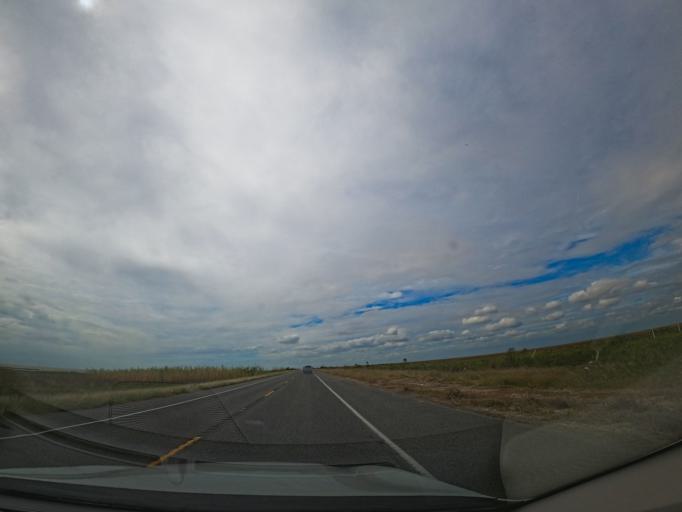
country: US
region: Louisiana
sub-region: Cameron Parish
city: Cameron
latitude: 29.7691
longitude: -93.4934
